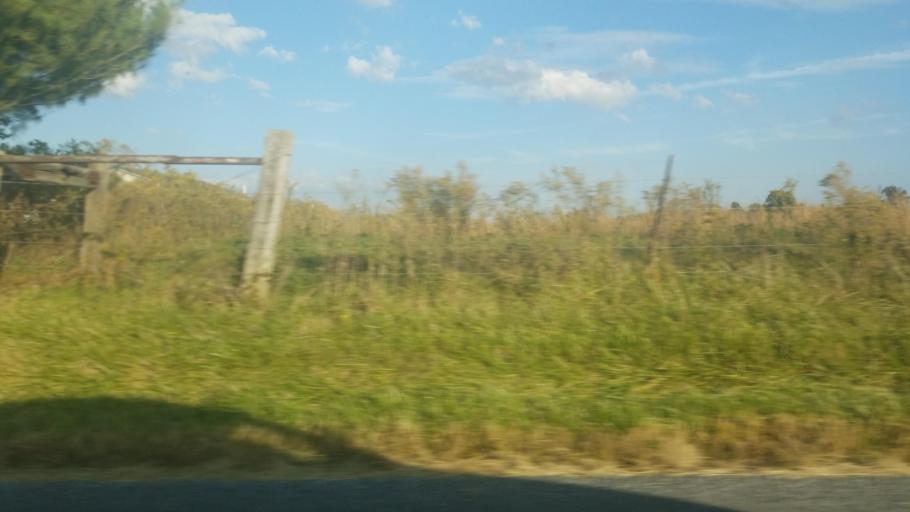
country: US
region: Illinois
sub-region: Saline County
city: Carrier Mills
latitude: 37.8014
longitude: -88.7117
